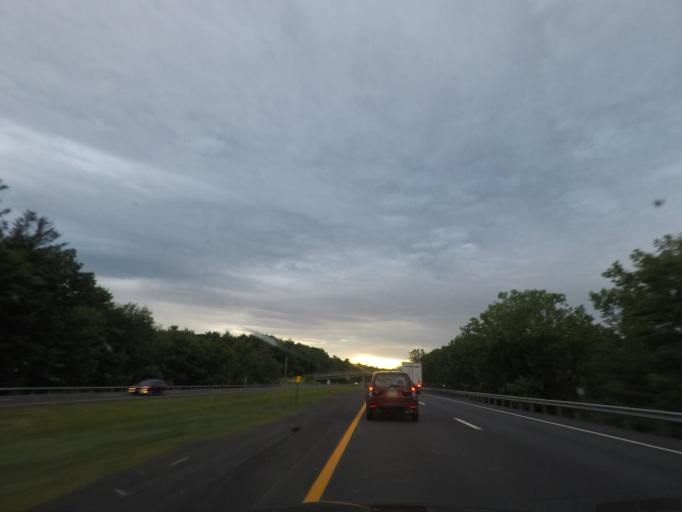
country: US
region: New York
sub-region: Rensselaer County
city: Nassau
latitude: 42.4458
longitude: -73.5638
